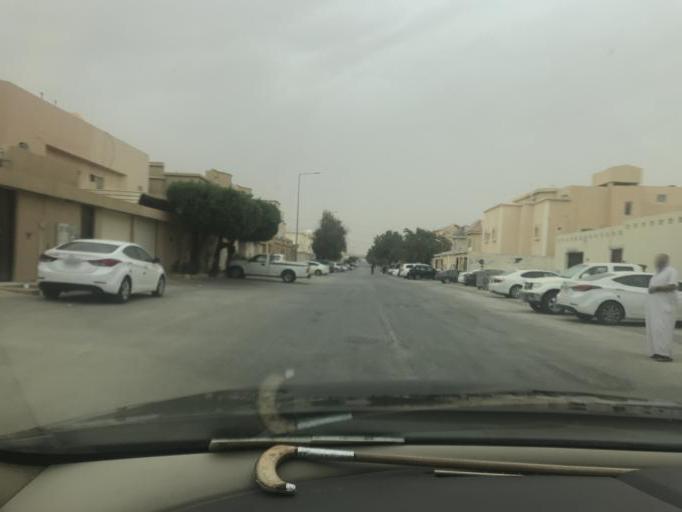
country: SA
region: Ar Riyad
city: Riyadh
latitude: 24.7928
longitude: 46.6936
